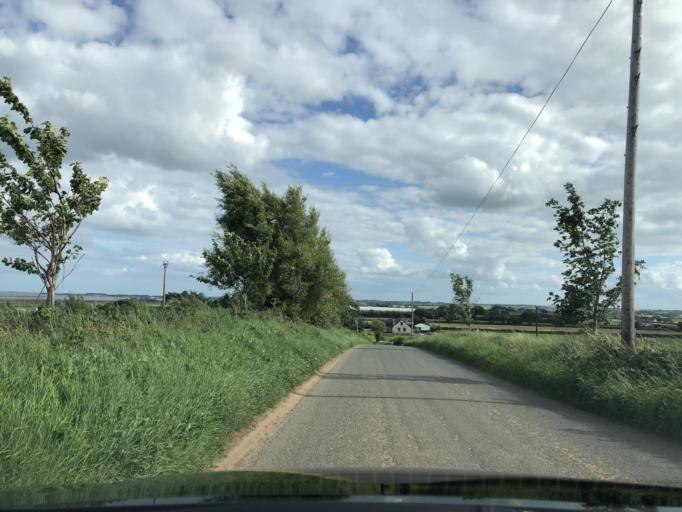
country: GB
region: Northern Ireland
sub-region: Ards District
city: Newtownards
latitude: 54.5630
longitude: -5.7102
